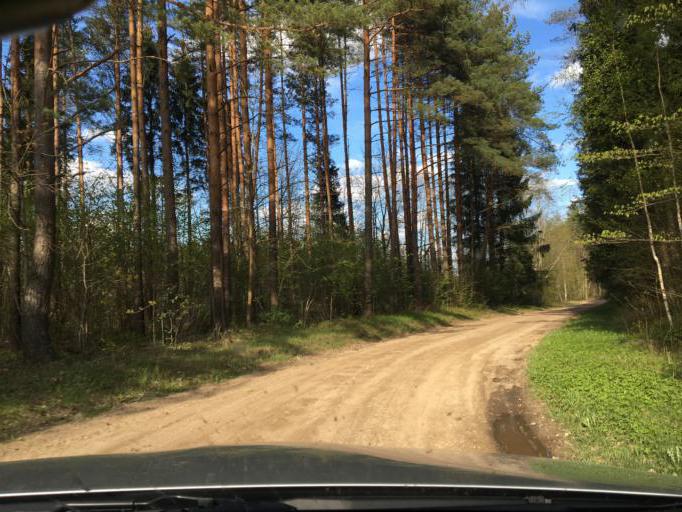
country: LV
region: Ozolnieku
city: Ozolnieki
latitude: 56.6661
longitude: 23.8721
